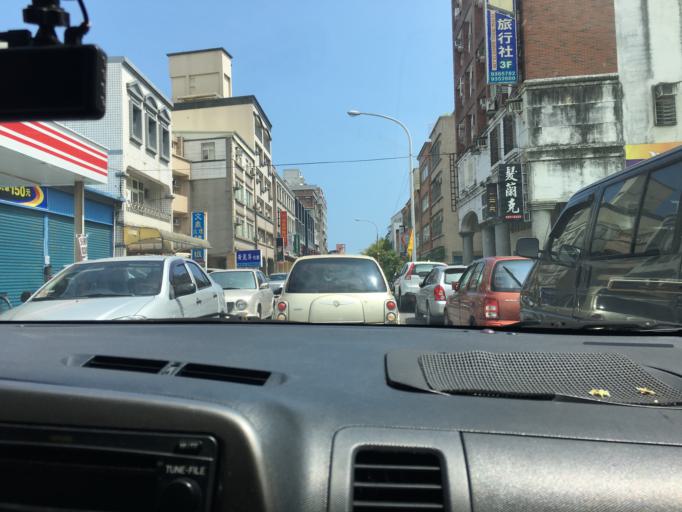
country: TW
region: Taiwan
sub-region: Yilan
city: Yilan
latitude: 24.7465
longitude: 121.7390
